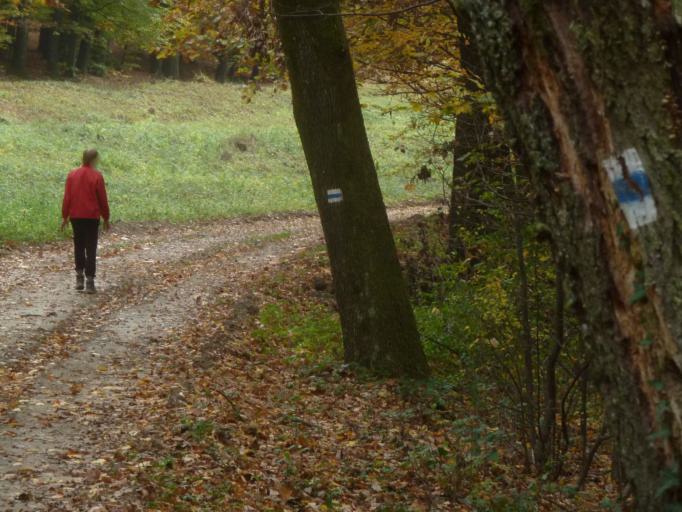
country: HU
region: Zala
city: Zalakomar
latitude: 46.5896
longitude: 17.0579
